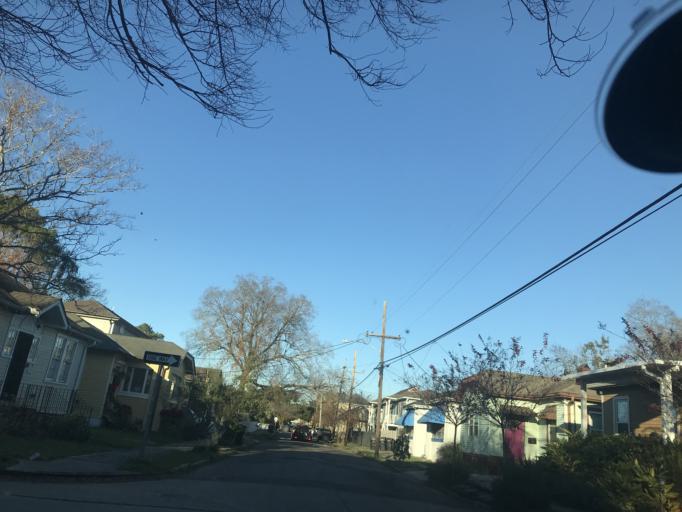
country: US
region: Louisiana
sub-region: Orleans Parish
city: New Orleans
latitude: 29.9532
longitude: -90.1060
